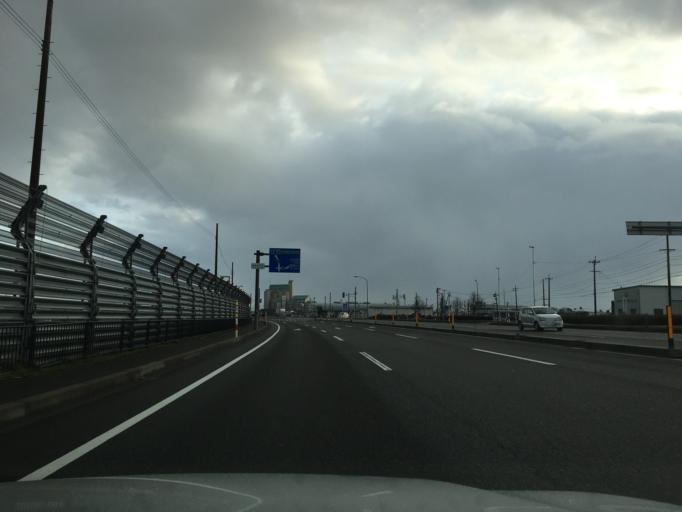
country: JP
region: Yamagata
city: Tsuruoka
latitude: 38.7235
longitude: 139.7720
